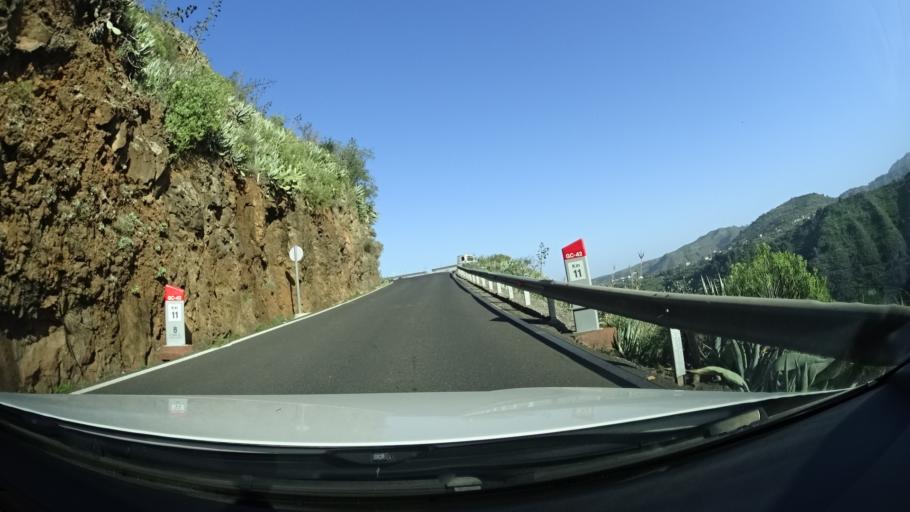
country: ES
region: Canary Islands
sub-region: Provincia de Las Palmas
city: Vega de San Mateo
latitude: 28.0240
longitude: -15.5487
